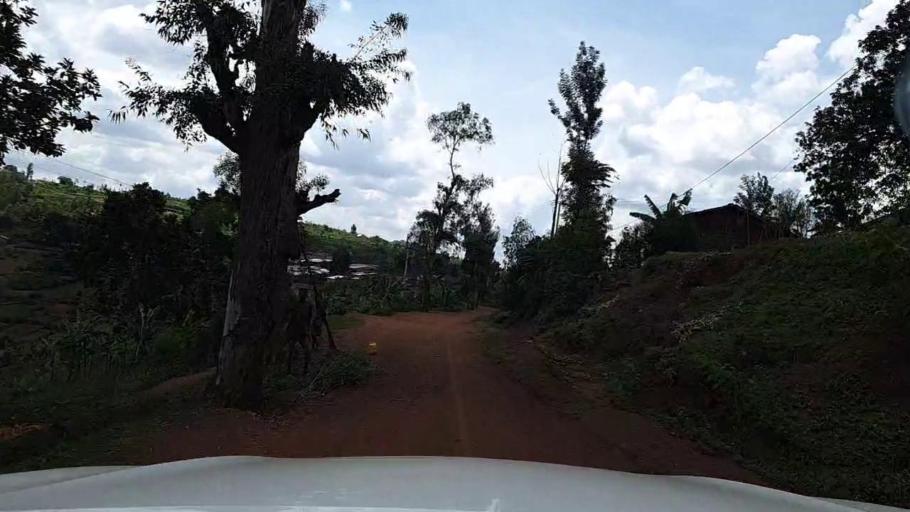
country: RW
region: Southern Province
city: Butare
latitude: -2.7603
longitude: 29.7462
